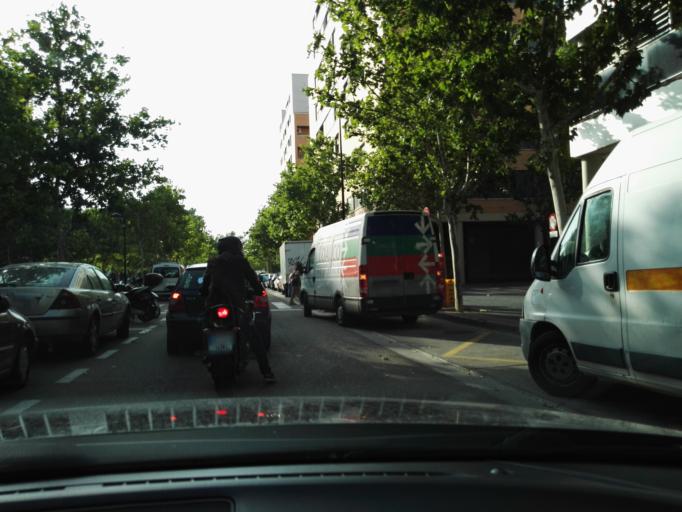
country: ES
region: Aragon
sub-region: Provincia de Zaragoza
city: Zaragoza
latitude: 41.6621
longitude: -0.8689
